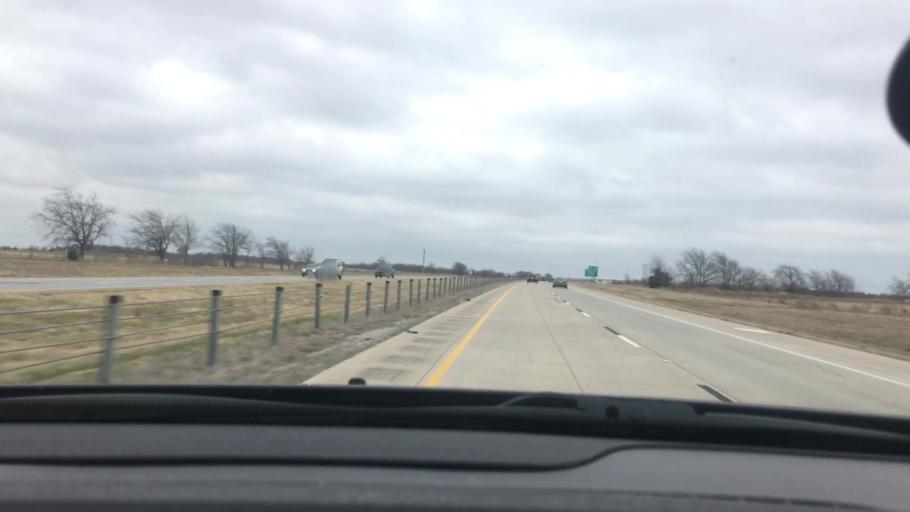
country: US
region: Oklahoma
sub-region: Bryan County
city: Durant
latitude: 34.0835
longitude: -96.3331
